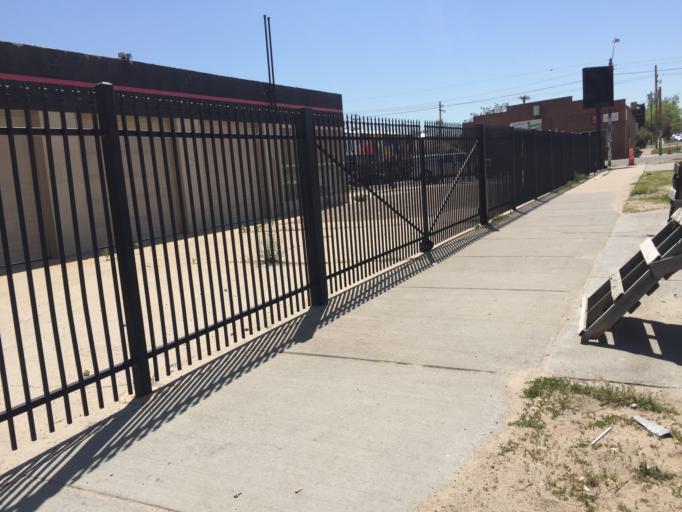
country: US
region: Colorado
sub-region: Denver County
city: Denver
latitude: 39.7618
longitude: -104.9821
